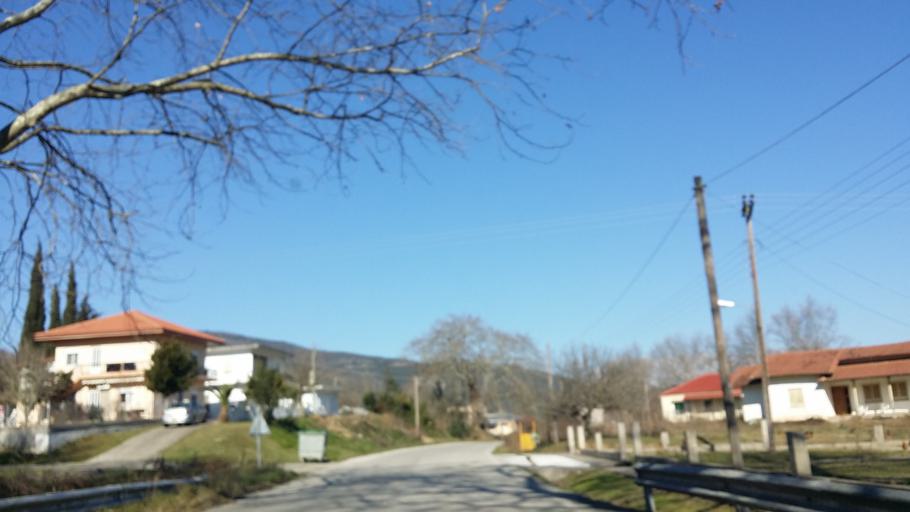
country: GR
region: West Greece
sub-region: Nomos Aitolias kai Akarnanias
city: Sardinia
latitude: 38.8633
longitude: 21.3378
